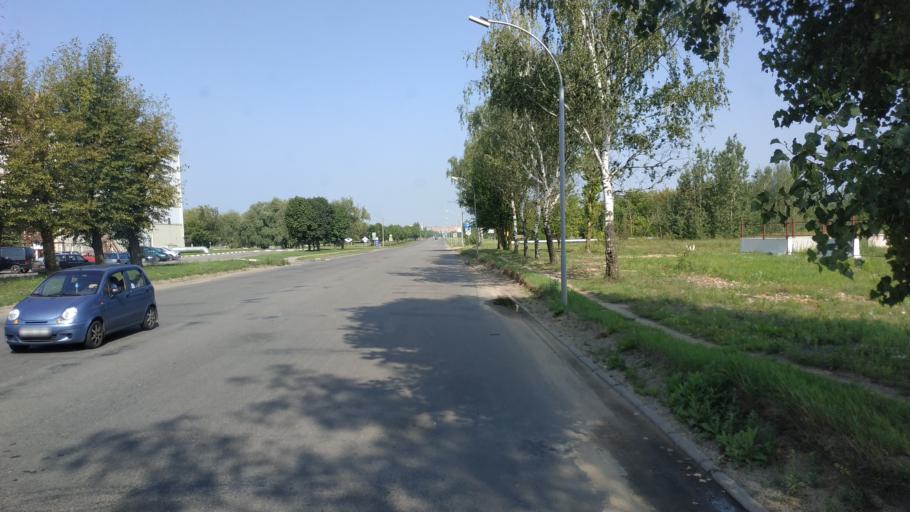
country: BY
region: Mogilev
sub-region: Mahilyowski Rayon
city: Veyno
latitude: 53.8567
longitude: 30.3300
